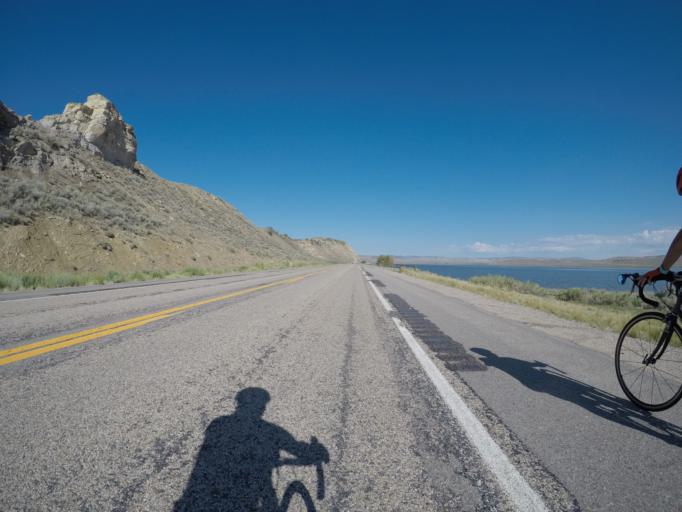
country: US
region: Wyoming
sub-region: Sublette County
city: Marbleton
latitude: 42.1118
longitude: -110.1451
